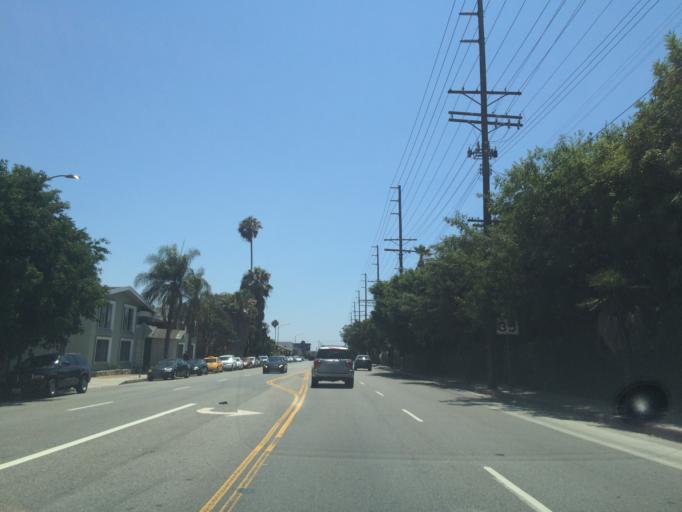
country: US
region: California
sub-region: Los Angeles County
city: Culver City
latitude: 34.0447
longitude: -118.3865
